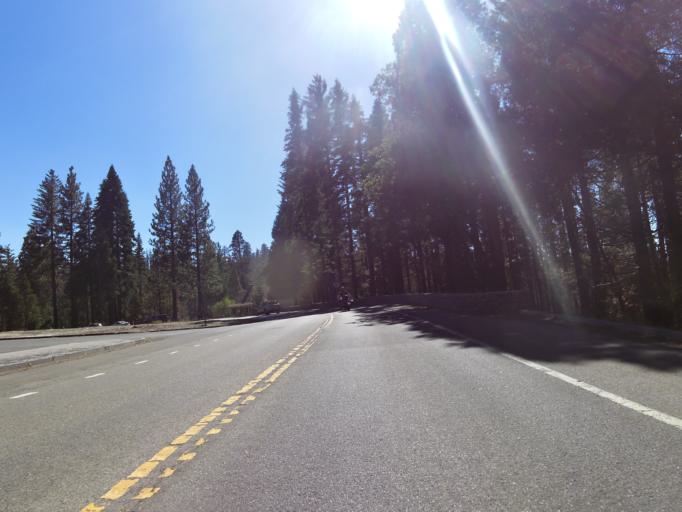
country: US
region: California
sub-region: Mariposa County
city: Yosemite Valley
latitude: 37.6531
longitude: -119.7029
